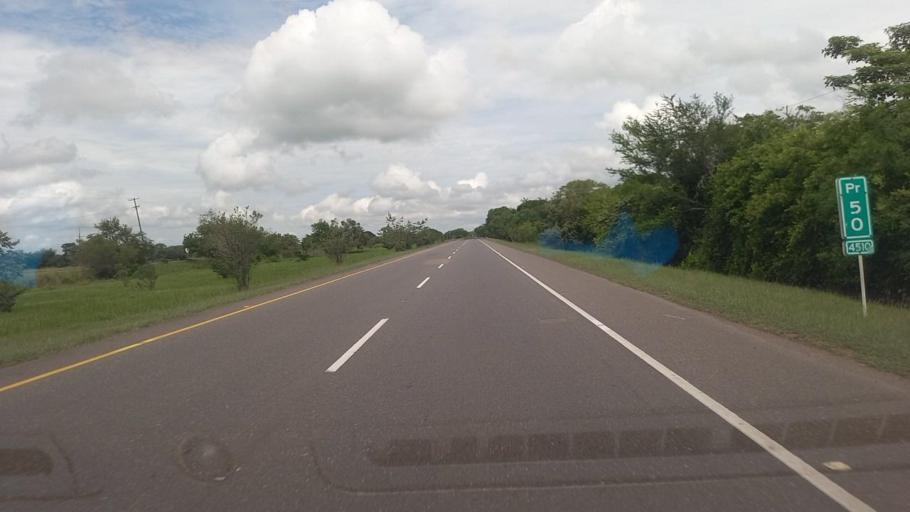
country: CO
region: Cundinamarca
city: Puerto Salgar
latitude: 5.5934
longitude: -74.6221
